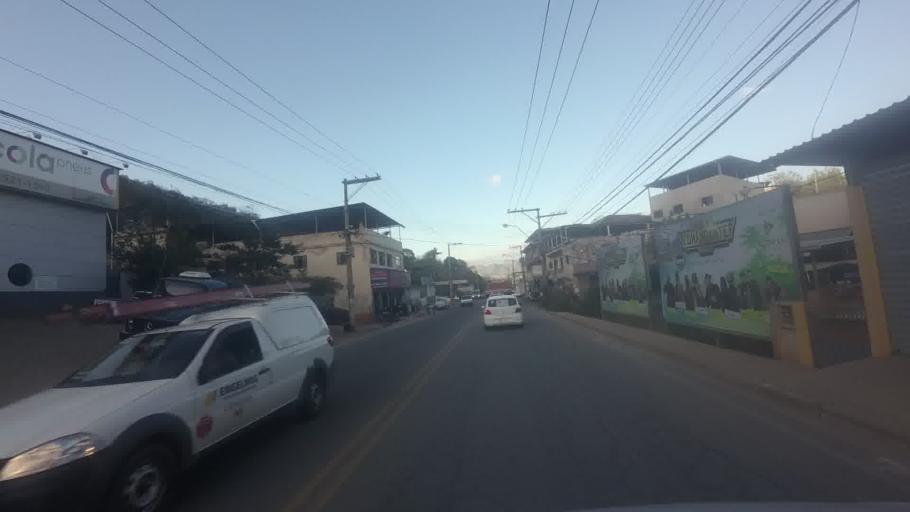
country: BR
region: Espirito Santo
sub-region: Cachoeiro De Itapemirim
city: Cachoeiro de Itapemirim
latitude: -20.8464
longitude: -41.1363
